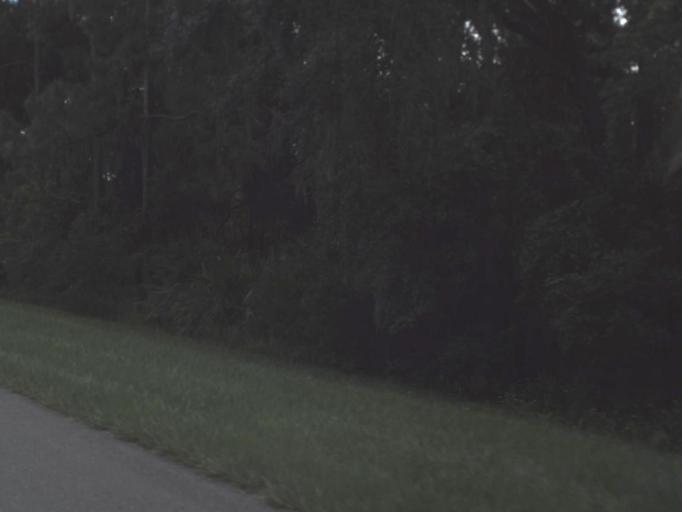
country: US
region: Florida
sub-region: Sarasota County
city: The Meadows
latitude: 27.4036
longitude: -82.3158
